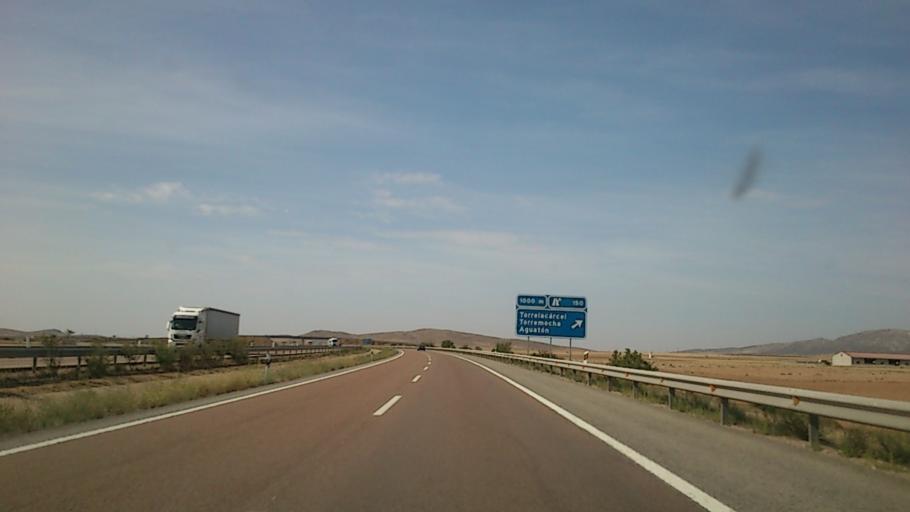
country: ES
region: Aragon
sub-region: Provincia de Teruel
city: Santa Eulalia
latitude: 40.6087
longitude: -1.2866
